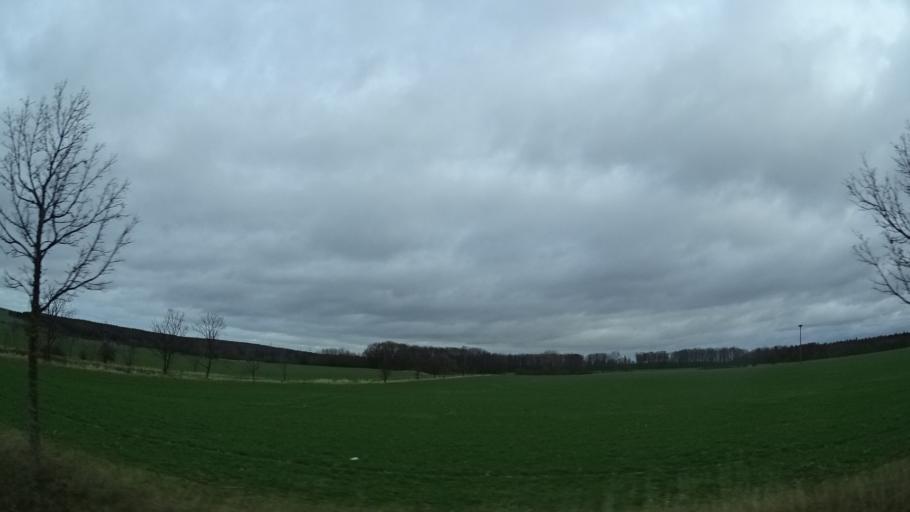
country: DE
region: Thuringia
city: Troistedt
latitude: 50.9327
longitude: 11.2460
